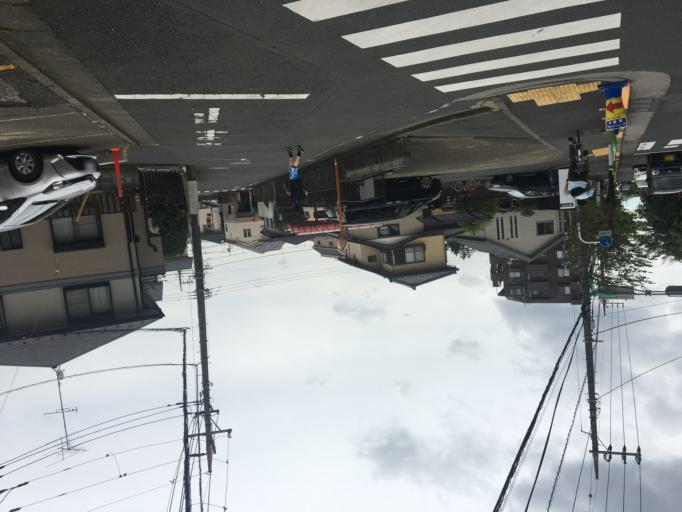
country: JP
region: Saitama
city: Shimotoda
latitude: 35.7567
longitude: 139.6713
